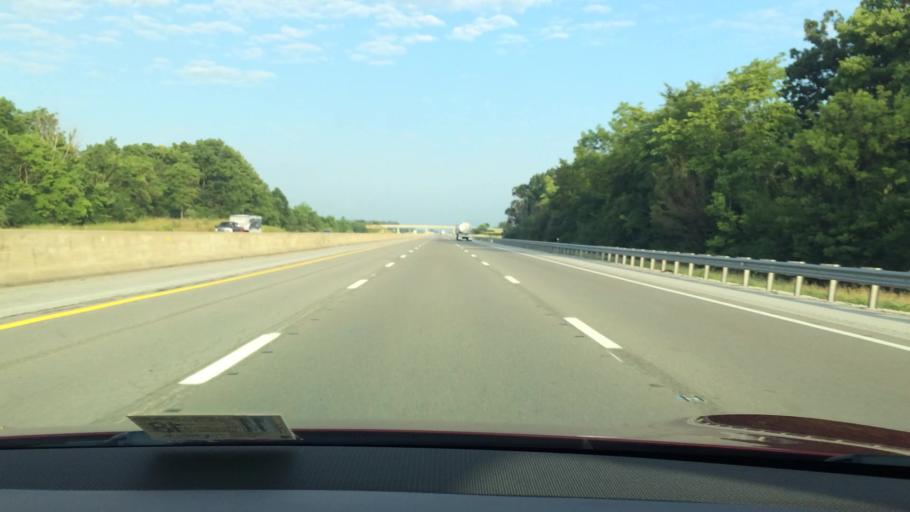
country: US
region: Ohio
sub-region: Huron County
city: Bellevue
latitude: 41.3496
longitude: -82.8369
